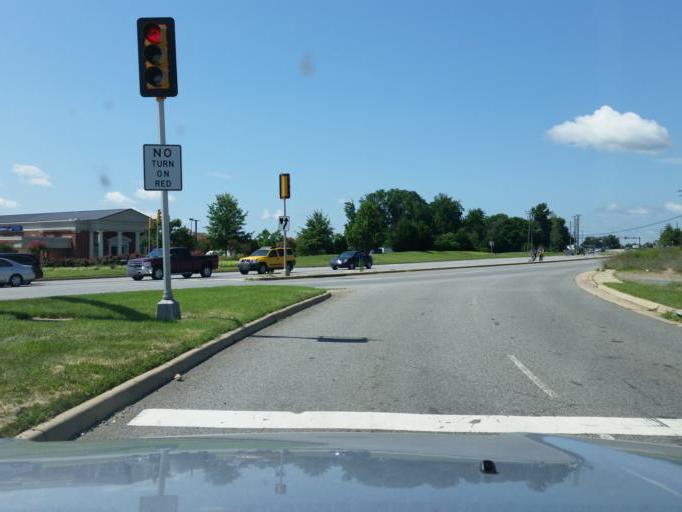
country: US
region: Virginia
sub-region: Stafford County
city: Falmouth
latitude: 38.3096
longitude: -77.5140
